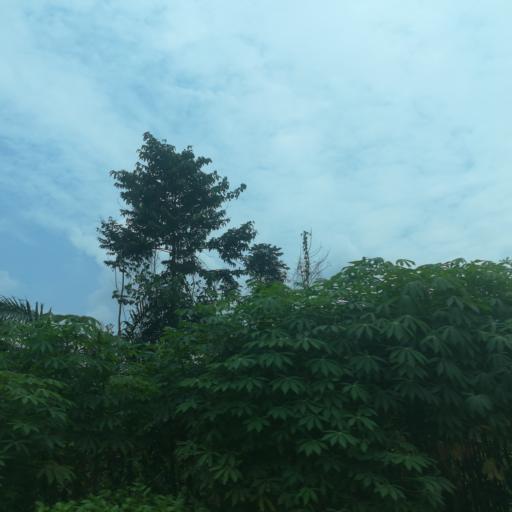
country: NG
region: Lagos
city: Ejirin
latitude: 6.6598
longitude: 3.8168
